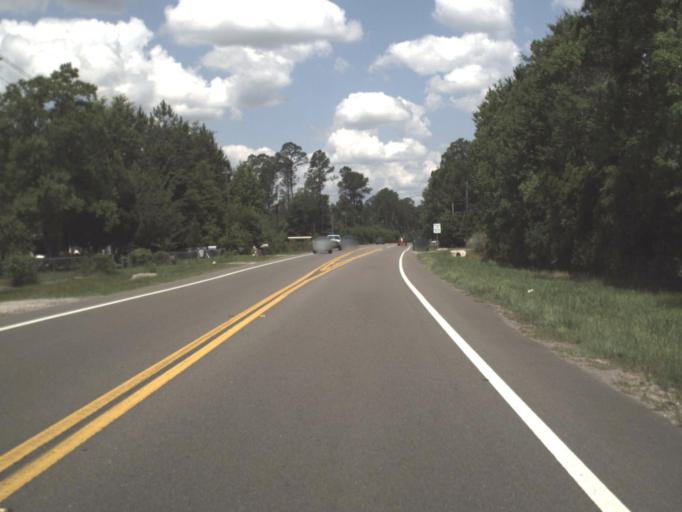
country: US
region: Florida
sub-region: Nassau County
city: Callahan
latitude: 30.5507
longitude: -81.7969
